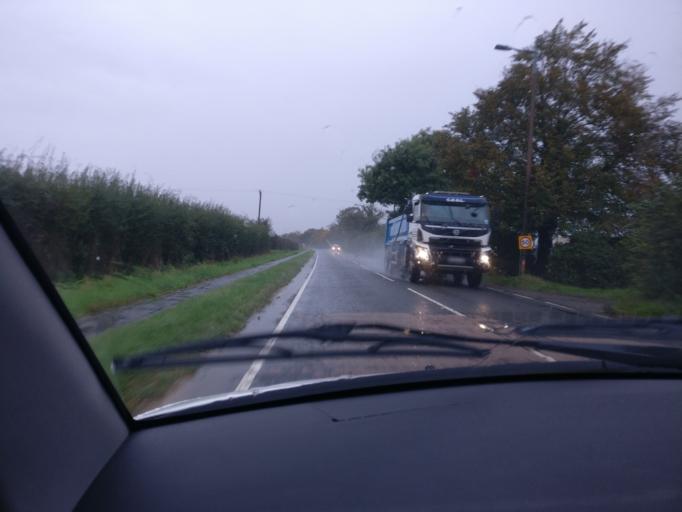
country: GB
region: England
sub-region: Lincolnshire
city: Bourne
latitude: 52.7392
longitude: -0.3673
